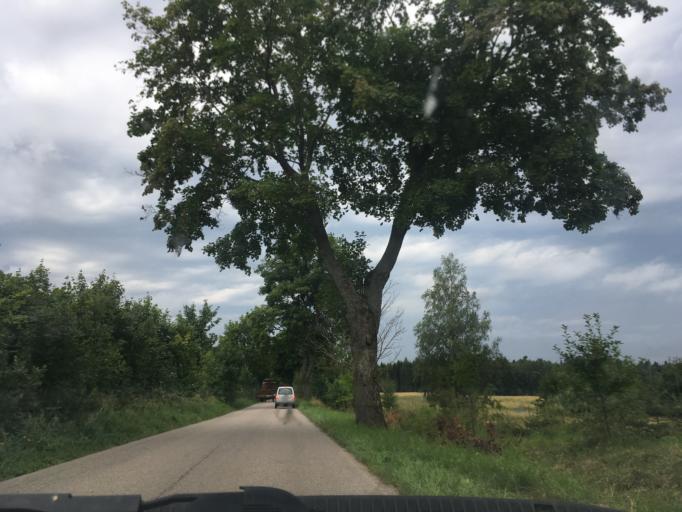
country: PL
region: Warmian-Masurian Voivodeship
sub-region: Powiat wegorzewski
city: Pozezdrze
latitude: 54.1200
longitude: 21.8132
